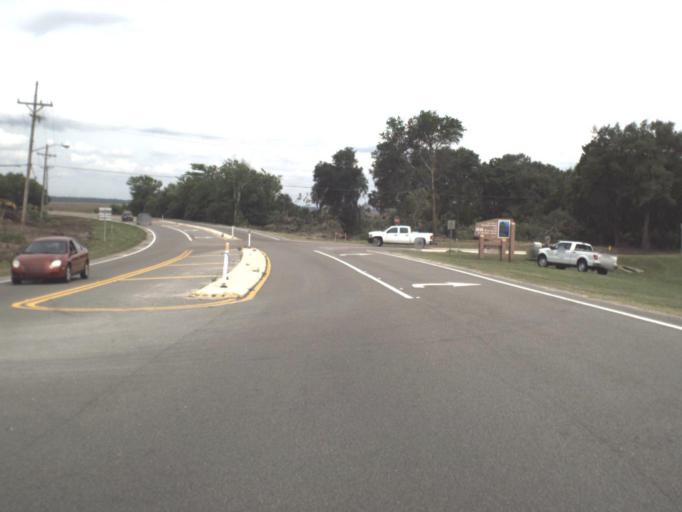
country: US
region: Florida
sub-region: Duval County
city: Atlantic Beach
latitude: 30.3956
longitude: -81.4612
